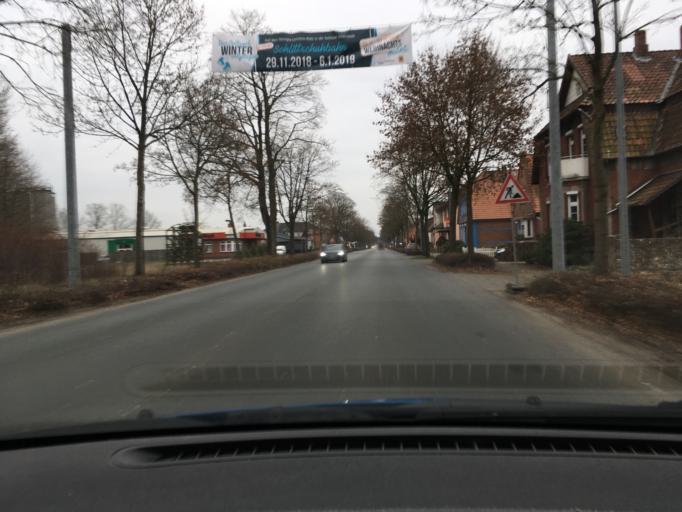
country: DE
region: Lower Saxony
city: Soltau
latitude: 52.9777
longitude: 9.8486
